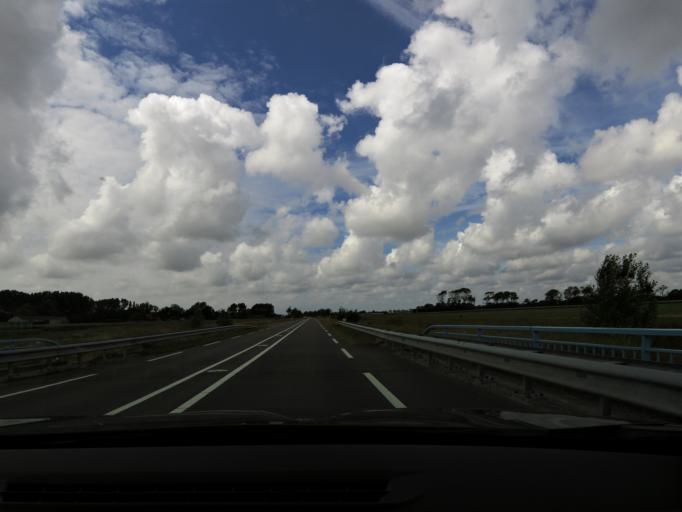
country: NL
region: Zeeland
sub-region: Gemeente Vlissingen
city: Vlissingen
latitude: 51.4754
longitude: 3.5666
